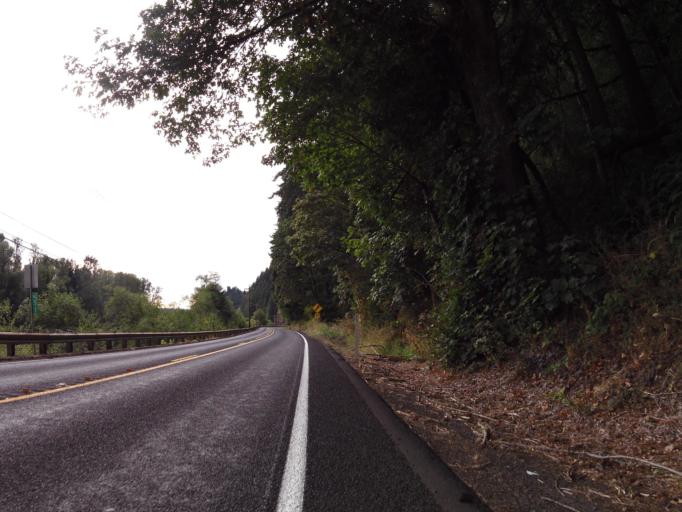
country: US
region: Washington
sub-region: Cowlitz County
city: West Longview
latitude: 46.1896
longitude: -123.1101
